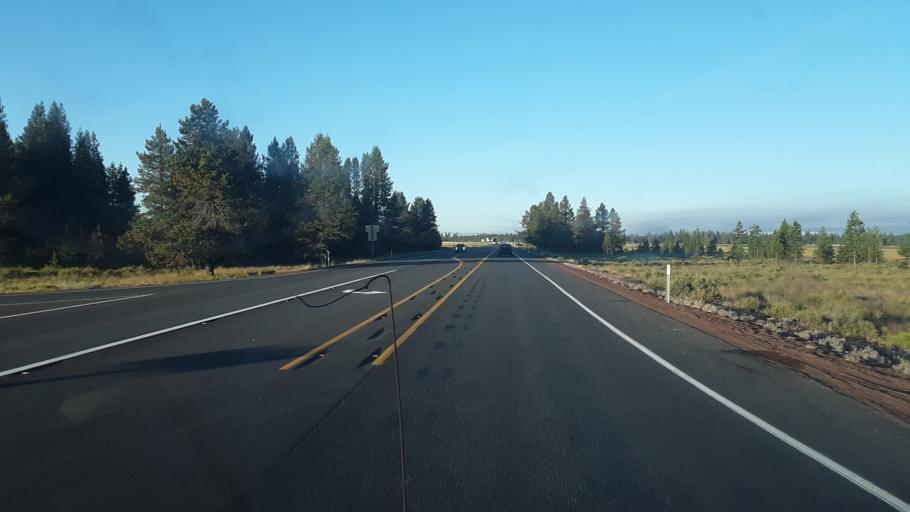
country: US
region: Oregon
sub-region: Deschutes County
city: Three Rivers
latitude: 43.7522
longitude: -121.4600
